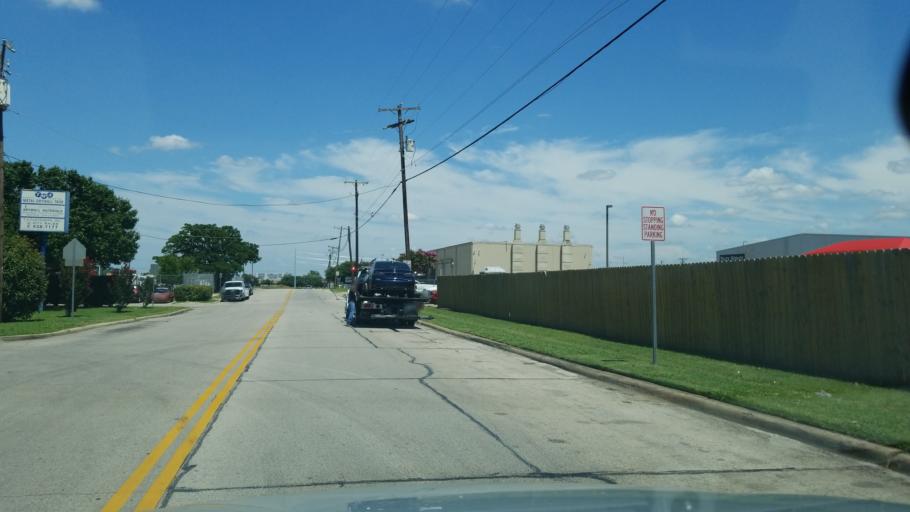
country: US
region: Texas
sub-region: Dallas County
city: Irving
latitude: 32.8175
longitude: -96.9243
